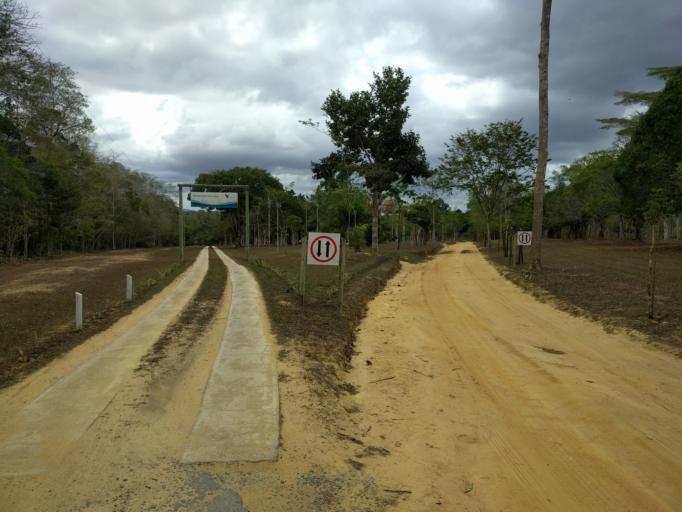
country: BR
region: Espirito Santo
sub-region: Linhares
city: Linhares
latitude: -19.1374
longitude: -40.0631
